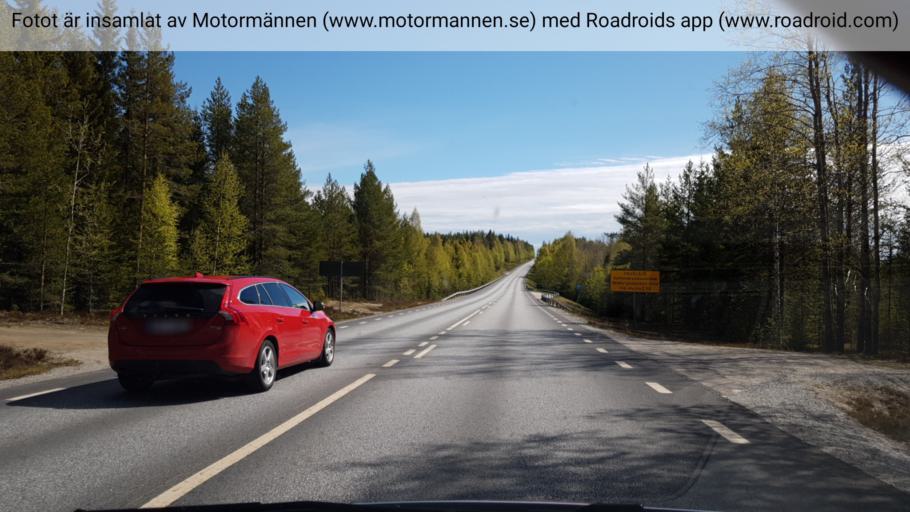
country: SE
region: Vaesterbotten
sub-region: Vannas Kommun
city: Vannasby
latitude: 64.0605
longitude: 19.9936
